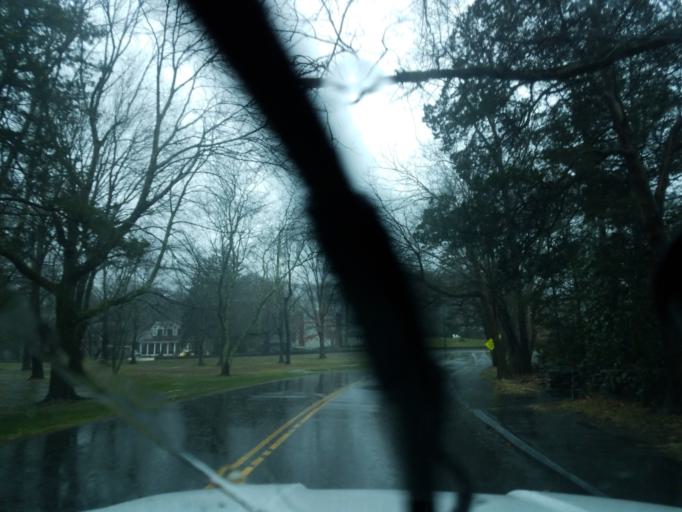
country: US
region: Connecticut
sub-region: Fairfield County
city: Darien
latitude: 41.0830
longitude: -73.4843
